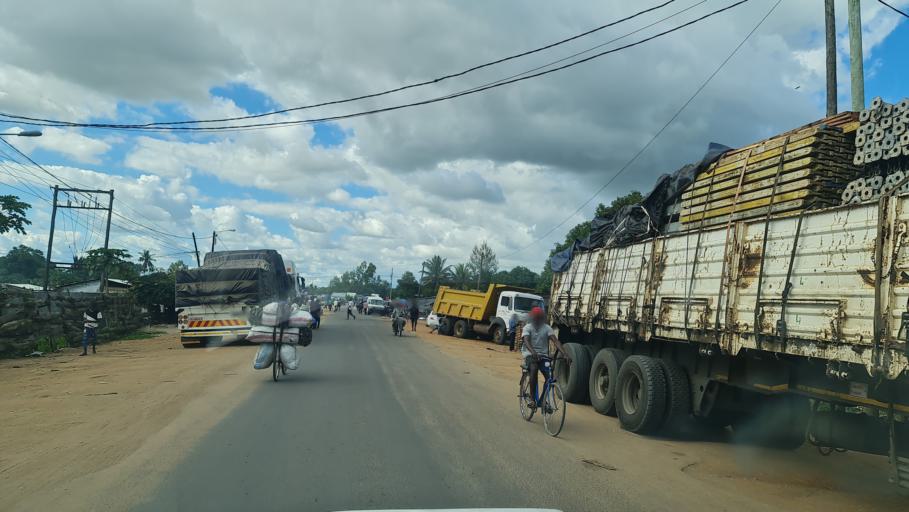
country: MZ
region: Zambezia
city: Quelimane
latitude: -17.5964
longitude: 36.8120
